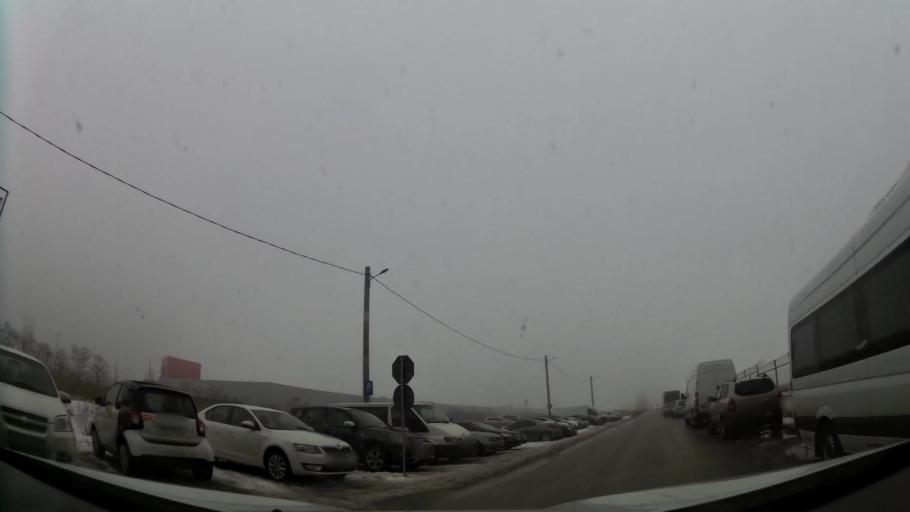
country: RO
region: Ilfov
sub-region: Comuna Chiajna
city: Chiajna
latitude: 44.4417
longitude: 25.9841
